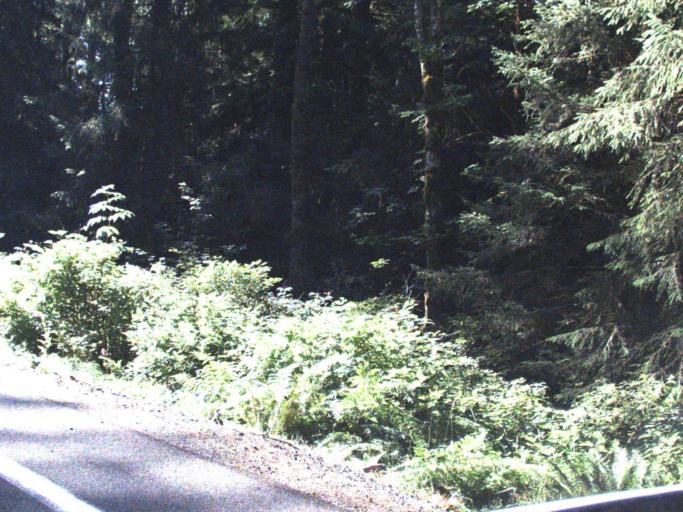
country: US
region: Washington
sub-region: King County
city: Enumclaw
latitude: 47.1610
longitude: -121.7353
